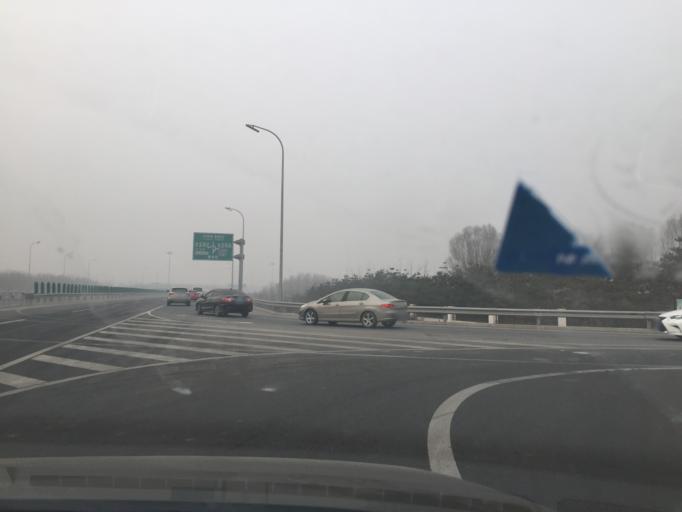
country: CN
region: Beijing
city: Qinghe
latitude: 40.0128
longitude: 116.3264
